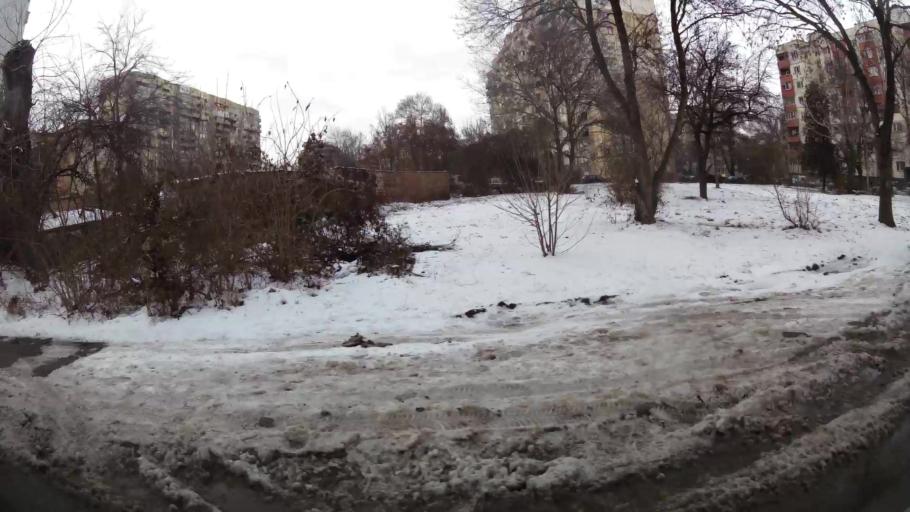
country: BG
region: Sofia-Capital
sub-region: Stolichna Obshtina
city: Sofia
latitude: 42.6999
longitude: 23.3560
